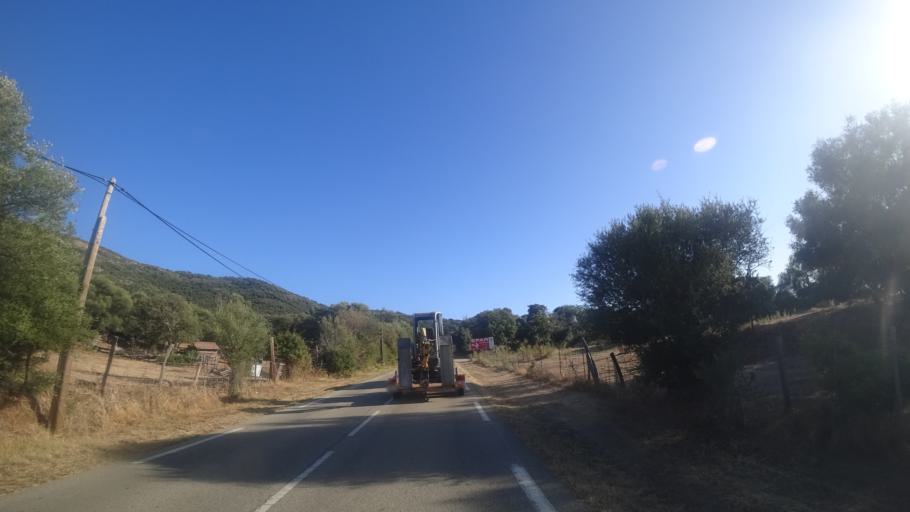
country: FR
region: Corsica
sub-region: Departement de la Corse-du-Sud
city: Cargese
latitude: 42.1526
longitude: 8.6064
